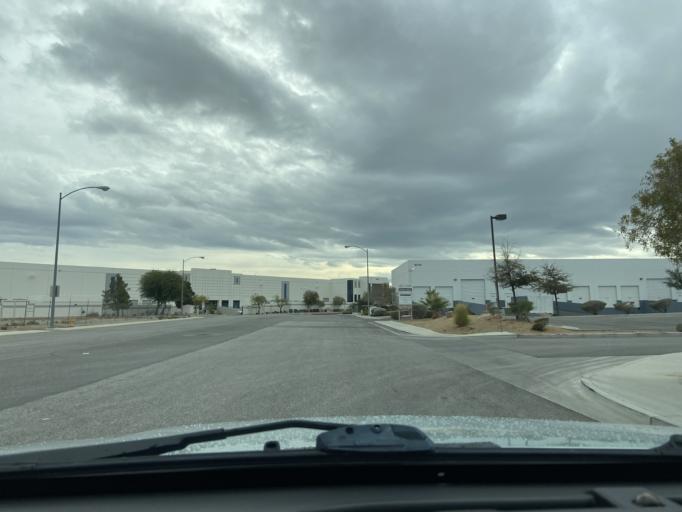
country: US
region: Nevada
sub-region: Clark County
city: North Las Vegas
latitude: 36.2428
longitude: -115.1079
